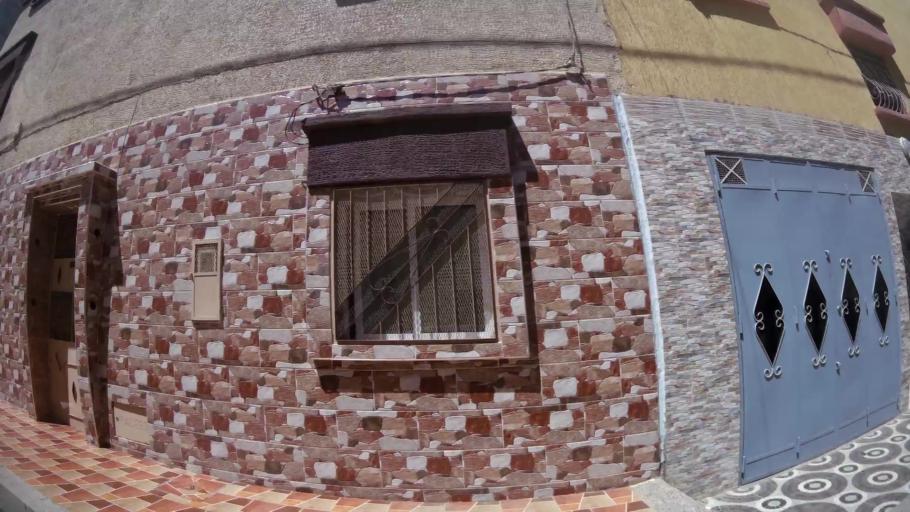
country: MA
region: Oriental
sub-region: Oujda-Angad
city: Oujda
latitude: 34.6651
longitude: -1.8840
